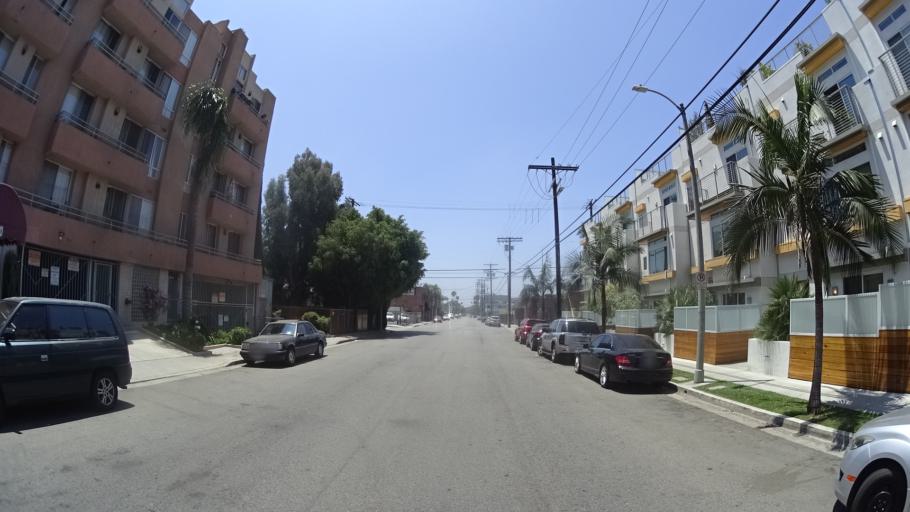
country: US
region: California
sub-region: Los Angeles County
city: Hollywood
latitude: 34.0931
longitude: -118.3364
